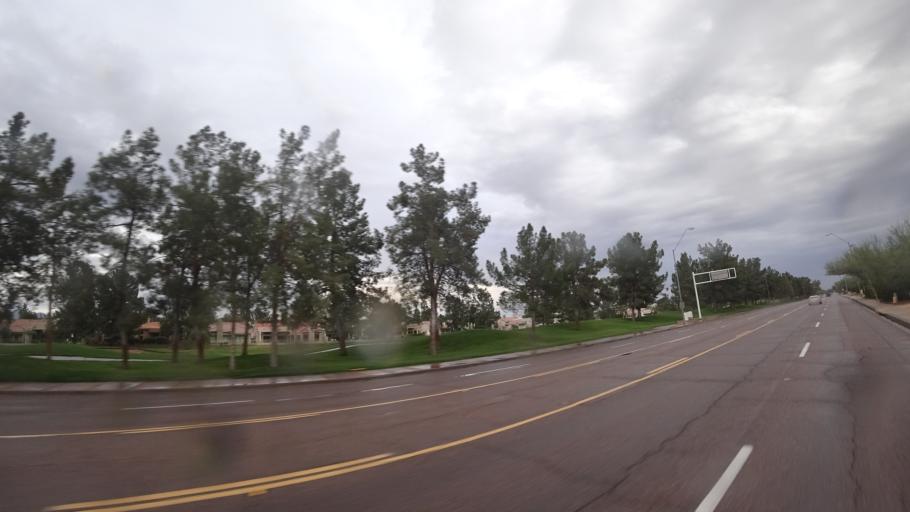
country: US
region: Arizona
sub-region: Maricopa County
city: Paradise Valley
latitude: 33.5940
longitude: -111.9087
